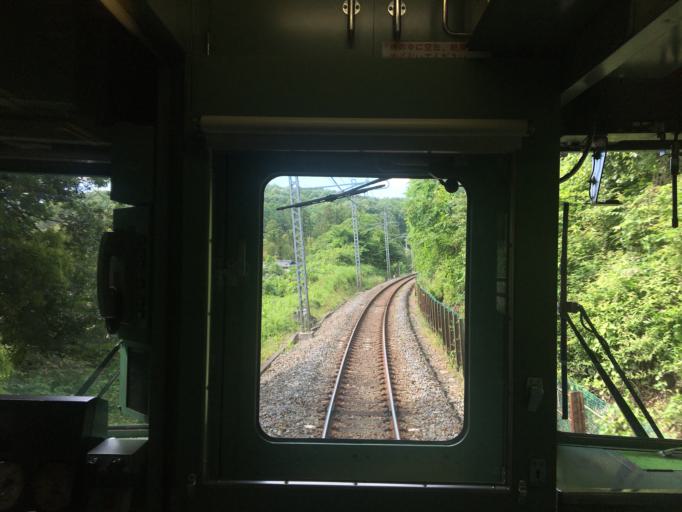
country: JP
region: Saitama
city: Yorii
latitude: 36.0961
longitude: 139.2348
